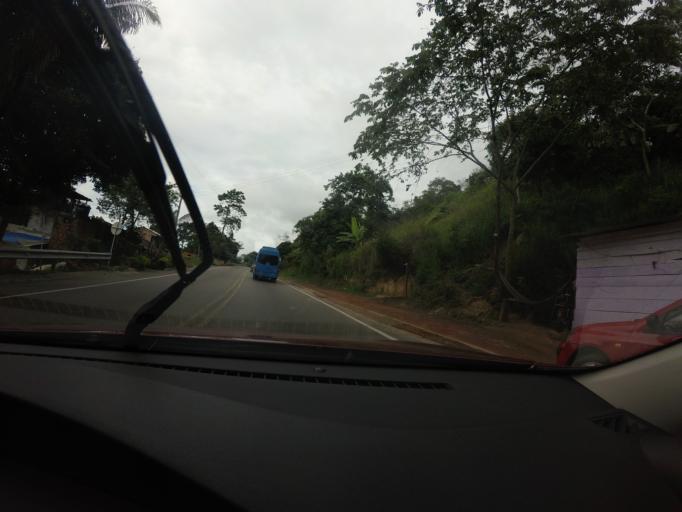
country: CO
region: Cundinamarca
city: Granada
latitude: 5.0629
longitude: -74.5746
